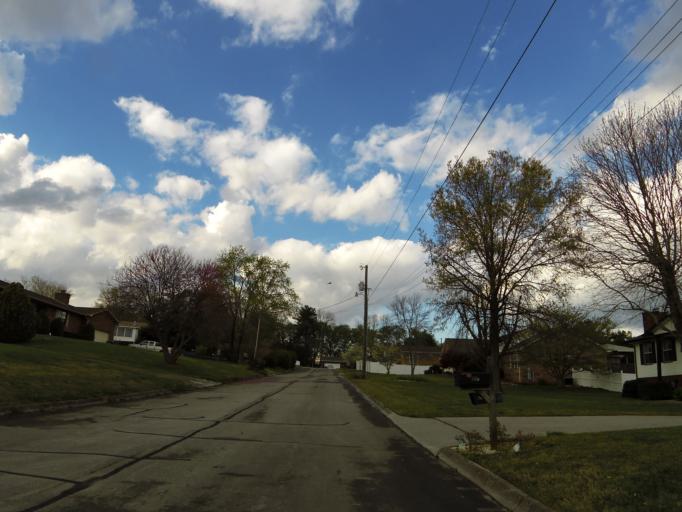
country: US
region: Tennessee
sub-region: Blount County
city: Maryville
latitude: 35.7255
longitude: -83.9744
